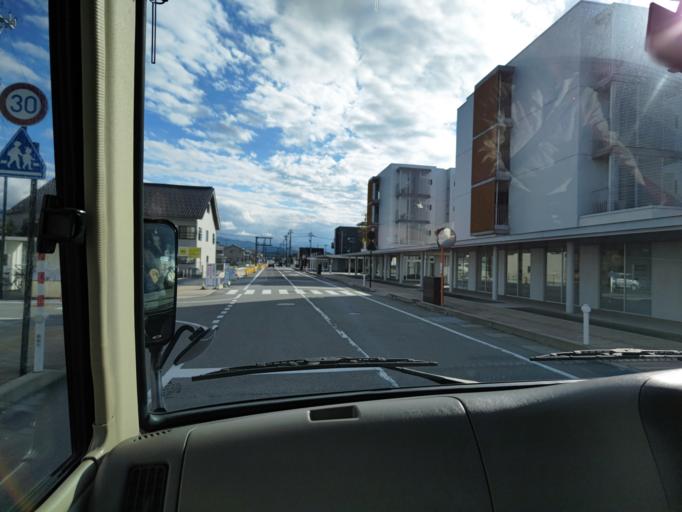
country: JP
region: Toyama
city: Nyuzen
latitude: 36.8782
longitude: 137.4466
